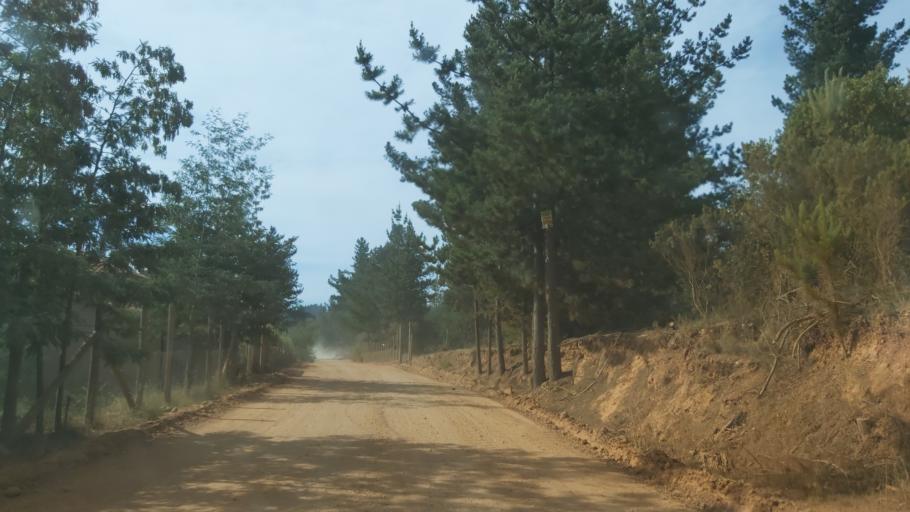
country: CL
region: Maule
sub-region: Provincia de Talca
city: Constitucion
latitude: -34.8445
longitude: -72.0382
